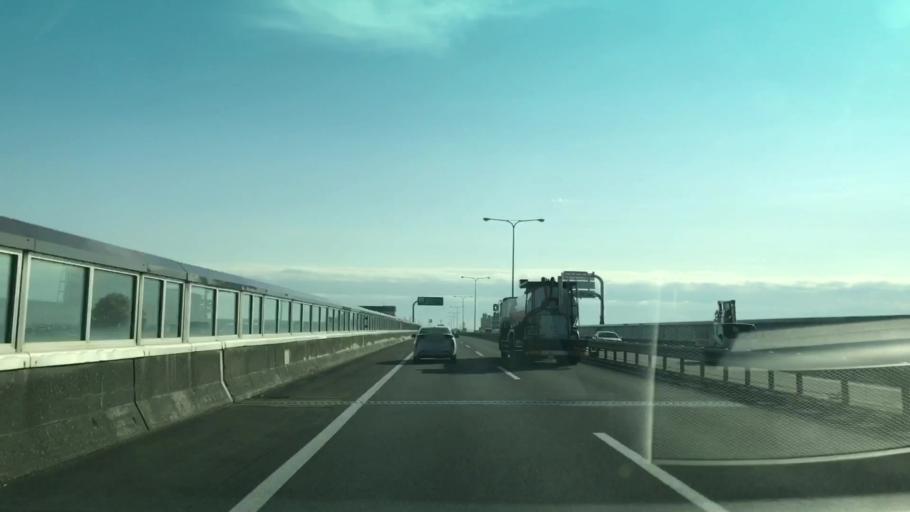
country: JP
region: Hokkaido
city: Sapporo
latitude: 43.1004
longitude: 141.3869
